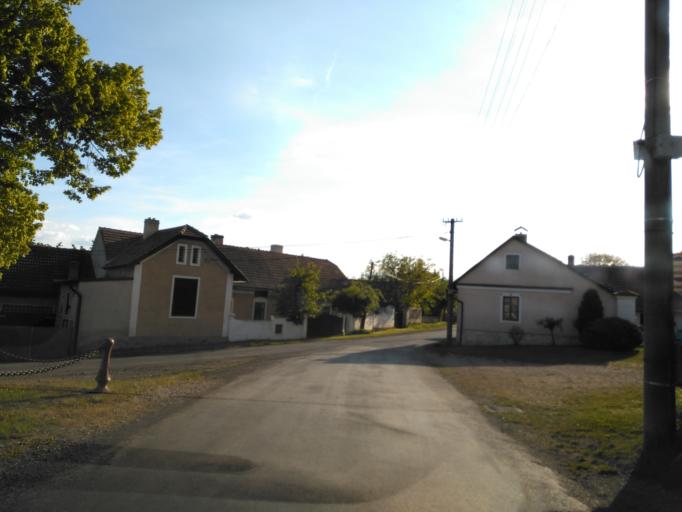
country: CZ
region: Central Bohemia
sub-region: Okres Beroun
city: Beroun
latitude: 49.8930
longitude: 14.0981
